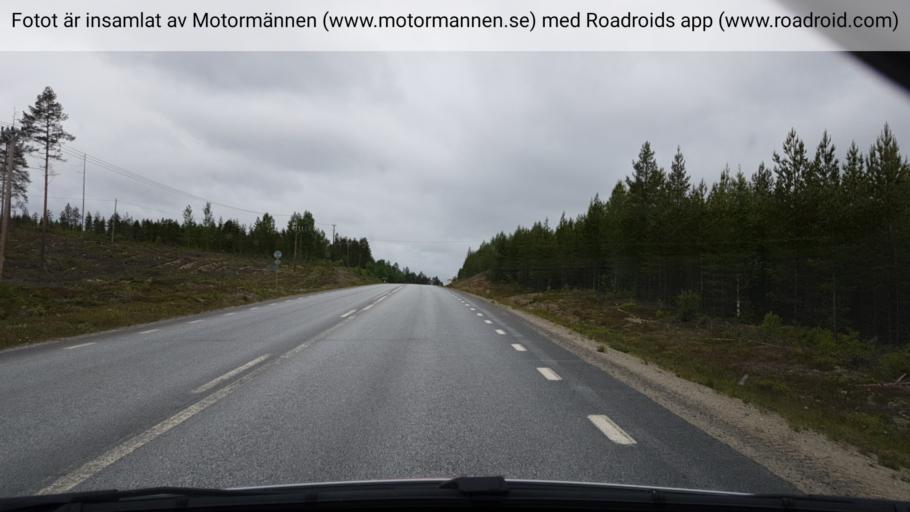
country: SE
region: Vaesterbotten
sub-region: Vannas Kommun
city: Vaennaes
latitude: 64.0287
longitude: 19.6919
